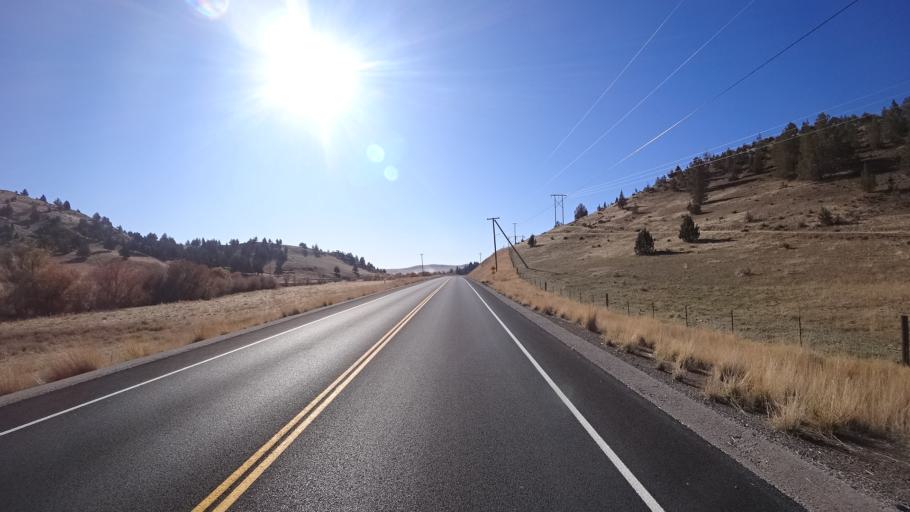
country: US
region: California
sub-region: Siskiyou County
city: Montague
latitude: 41.8629
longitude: -122.4642
